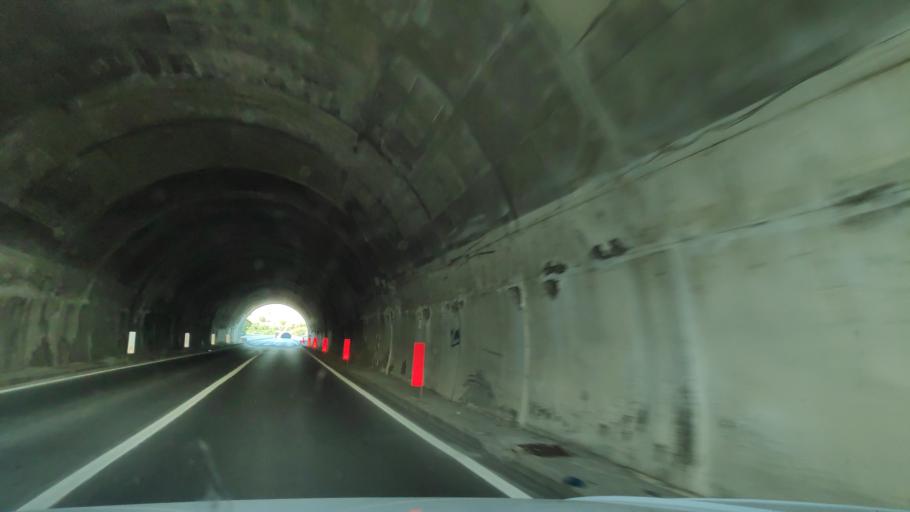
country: IT
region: Calabria
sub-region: Provincia di Reggio Calabria
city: Bova Marina
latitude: 37.9301
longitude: 15.9069
